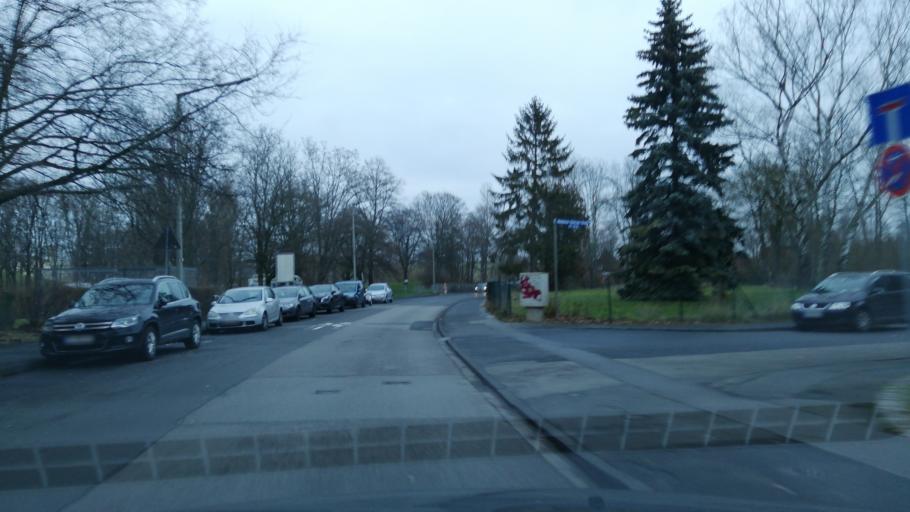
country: DE
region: Hesse
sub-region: Regierungsbezirk Kassel
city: Lohfelden
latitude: 51.2929
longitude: 9.5247
